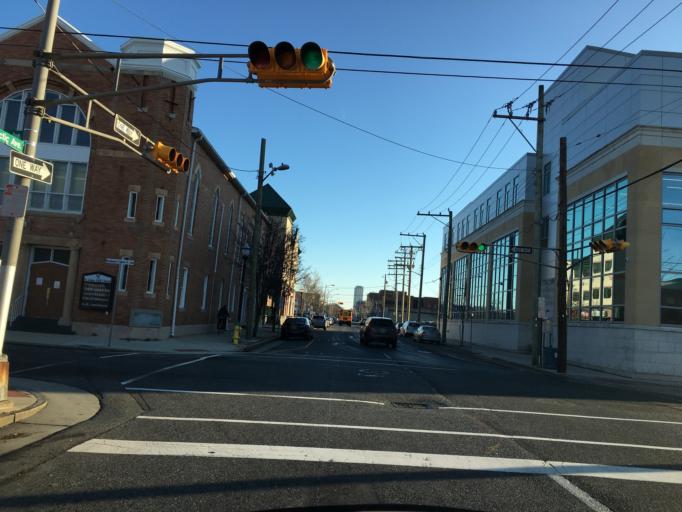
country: US
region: New Jersey
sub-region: Atlantic County
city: Atlantic City
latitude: 39.3631
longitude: -74.4306
